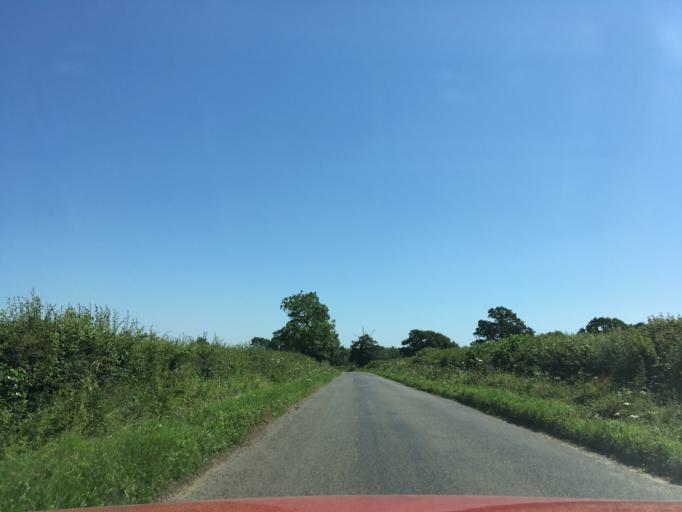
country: GB
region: England
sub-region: Milton Keynes
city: Calverton
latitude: 52.0035
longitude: -0.8560
